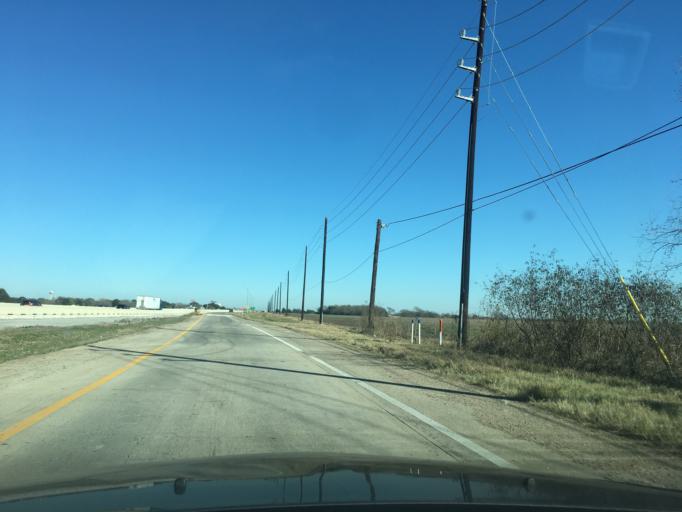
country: US
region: Texas
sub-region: Fort Bend County
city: Pleak
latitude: 29.4874
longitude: -95.9279
